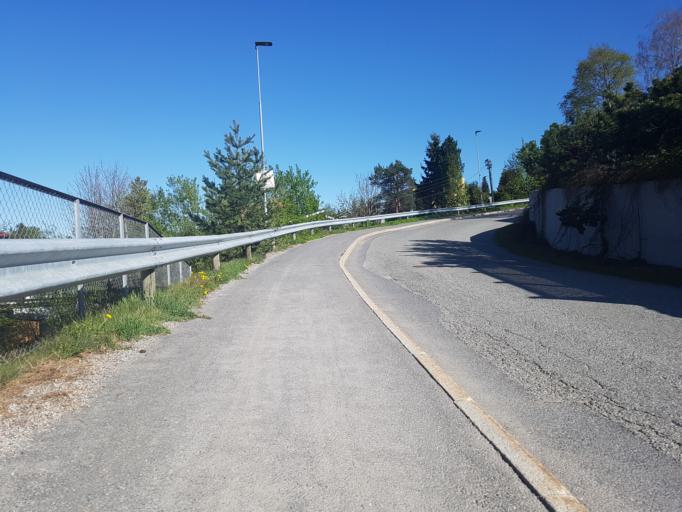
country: NO
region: Buskerud
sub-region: Drammen
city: Drammen
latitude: 59.7246
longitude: 10.2071
